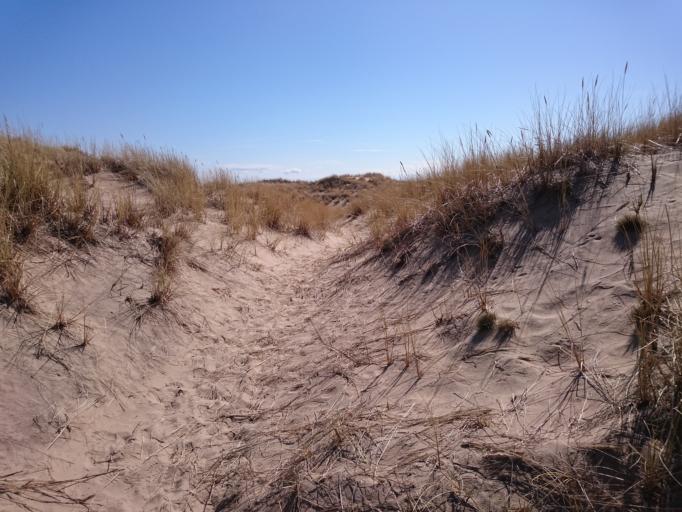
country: DK
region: North Denmark
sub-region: Frederikshavn Kommune
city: Skagen
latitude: 57.6930
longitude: 10.5273
